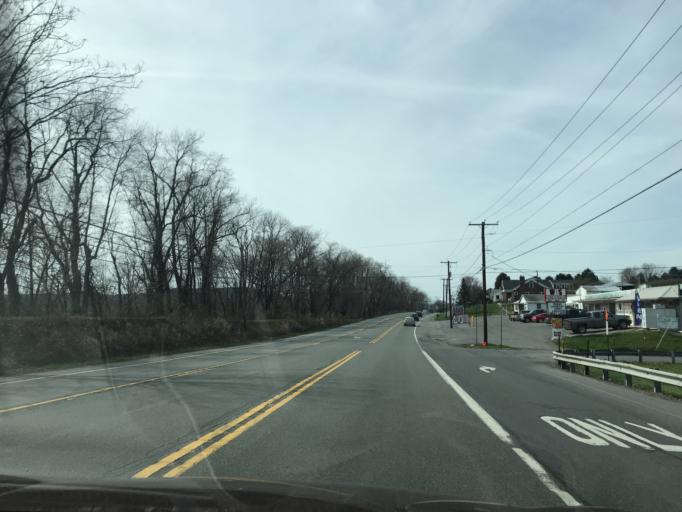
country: US
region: Pennsylvania
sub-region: Northumberland County
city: Northumberland
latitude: 40.9062
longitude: -76.8317
